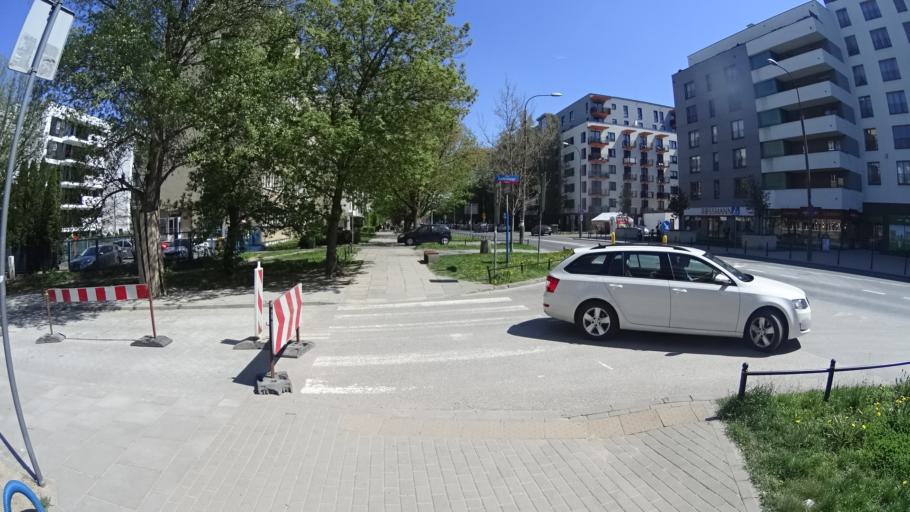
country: PL
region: Masovian Voivodeship
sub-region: Warszawa
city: Bemowo
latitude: 52.2218
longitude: 20.9328
